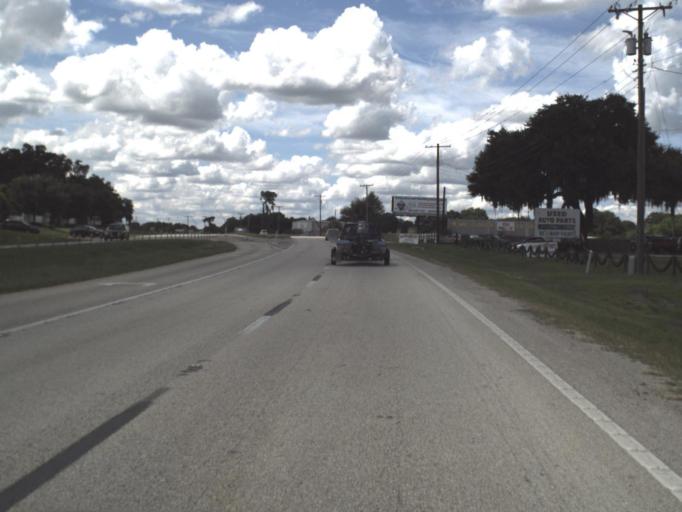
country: US
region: Florida
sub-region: Polk County
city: Willow Oak
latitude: 27.9255
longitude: -82.0326
